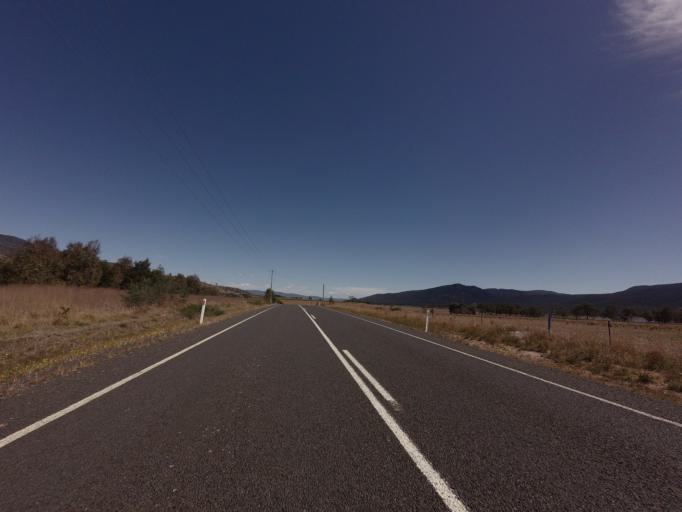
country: AU
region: Tasmania
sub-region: Break O'Day
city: St Helens
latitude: -41.7122
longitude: 147.8395
